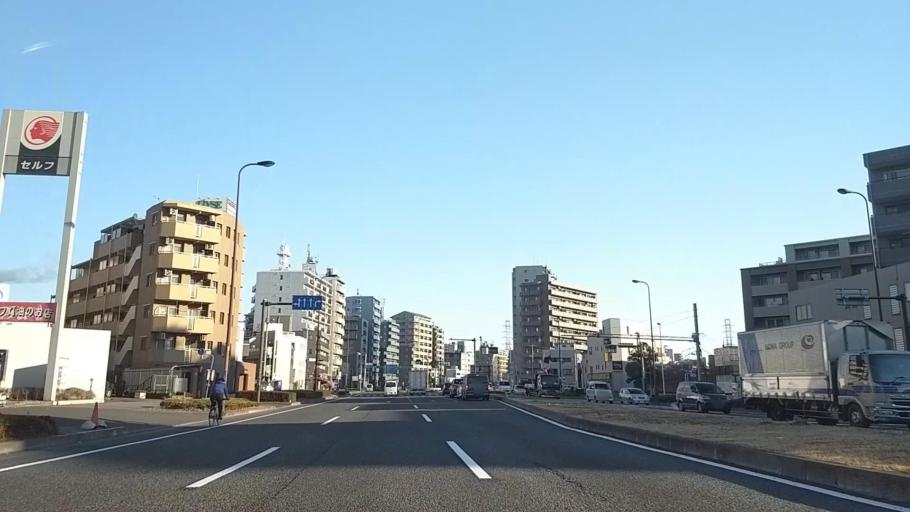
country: JP
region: Kanagawa
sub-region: Kawasaki-shi
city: Kawasaki
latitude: 35.5180
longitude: 139.6886
